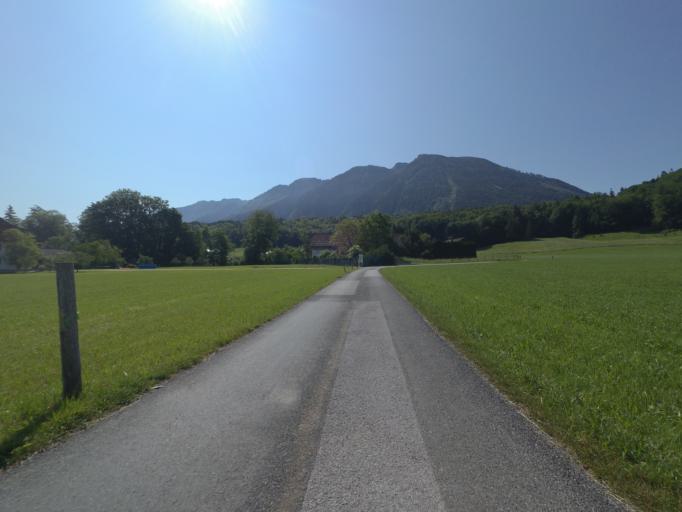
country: DE
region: Bavaria
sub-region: Upper Bavaria
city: Piding
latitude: 47.7374
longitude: 12.9314
